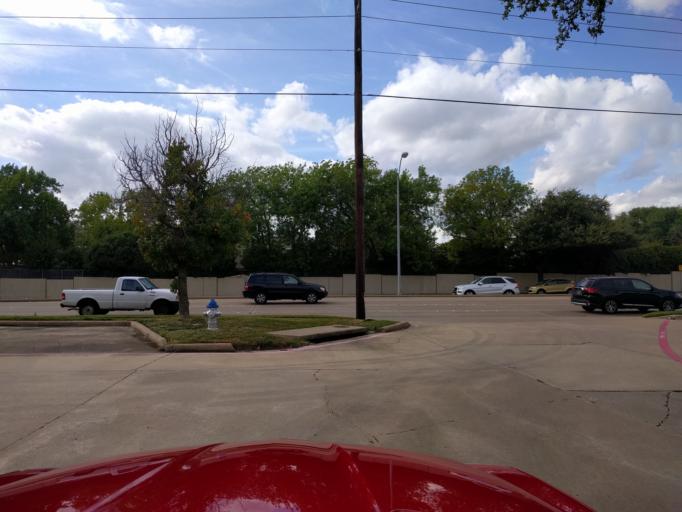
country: US
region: Texas
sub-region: Collin County
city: Plano
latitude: 32.9843
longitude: -96.6821
